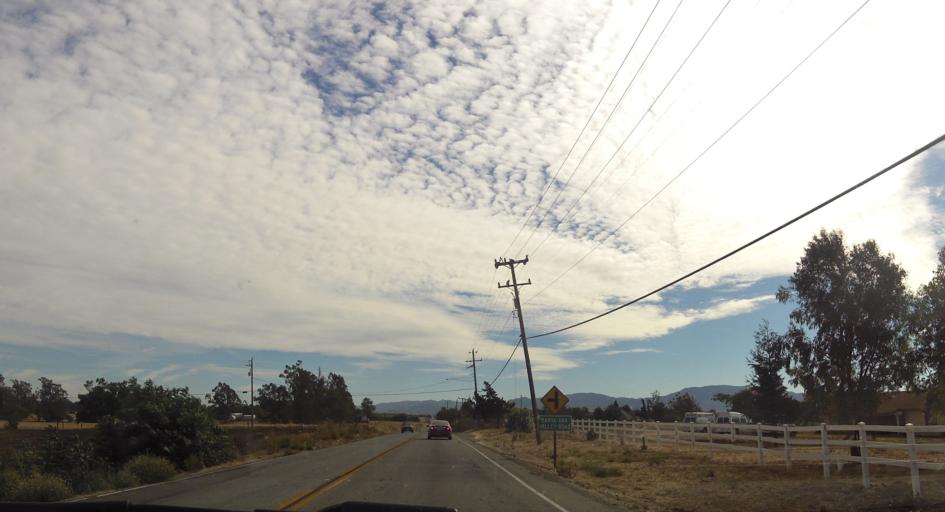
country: US
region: California
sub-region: San Benito County
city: Hollister
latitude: 36.8622
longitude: -121.3637
